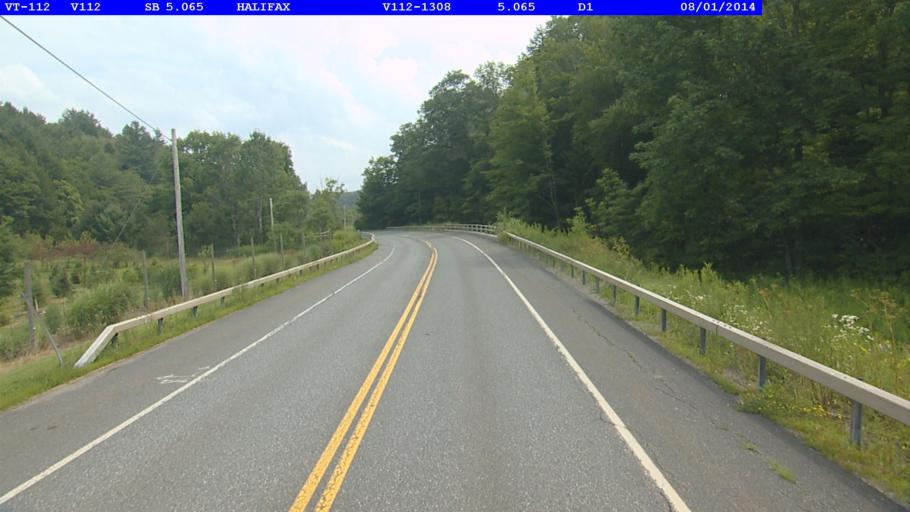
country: US
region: Massachusetts
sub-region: Franklin County
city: Colrain
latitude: 42.7690
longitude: -72.7986
